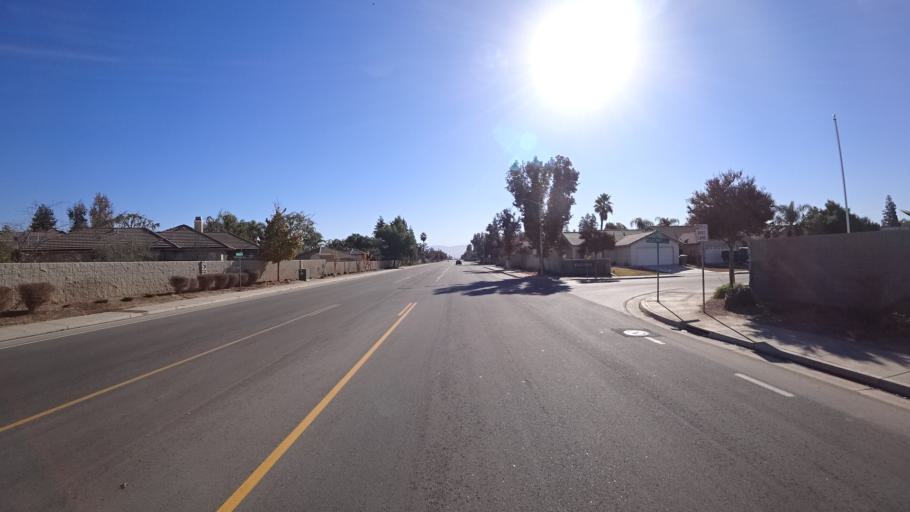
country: US
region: California
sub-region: Kern County
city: Greenfield
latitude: 35.2792
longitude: -119.0478
